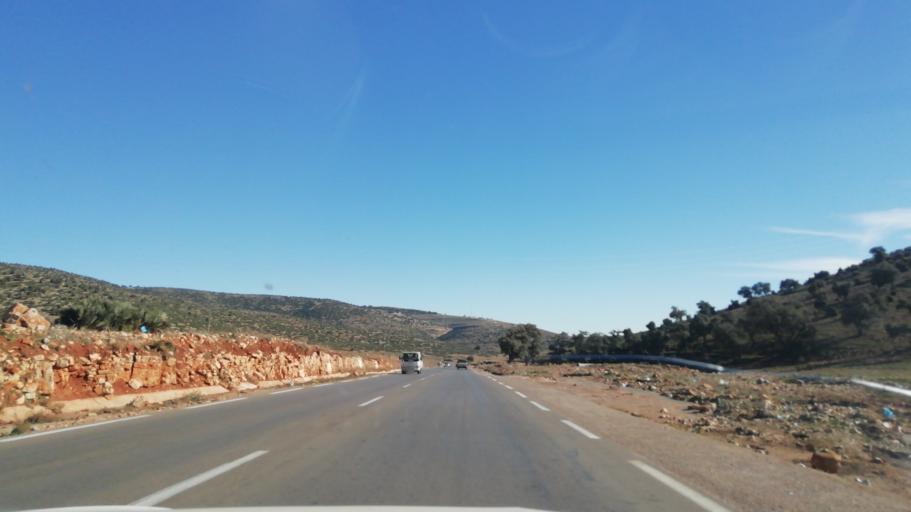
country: DZ
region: Tlemcen
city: Sebdou
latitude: 34.7155
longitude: -1.3294
